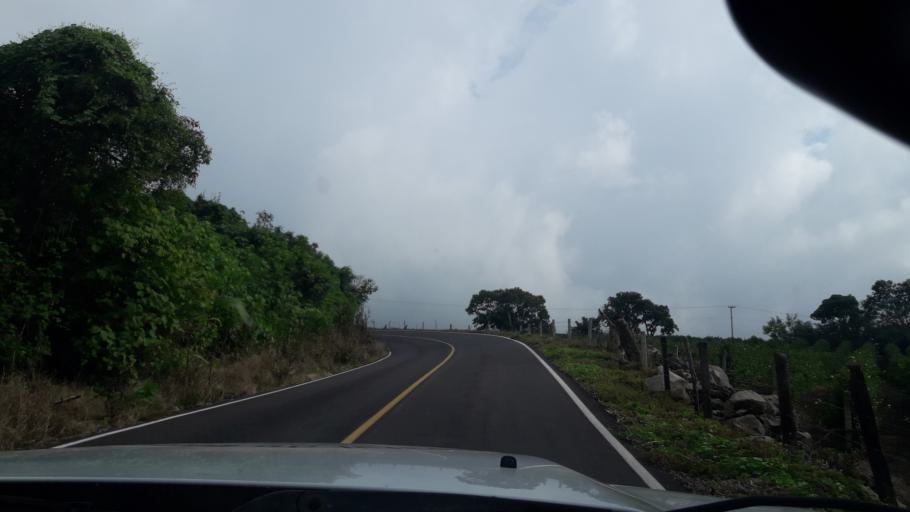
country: MX
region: Colima
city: Queseria
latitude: 19.4086
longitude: -103.6375
